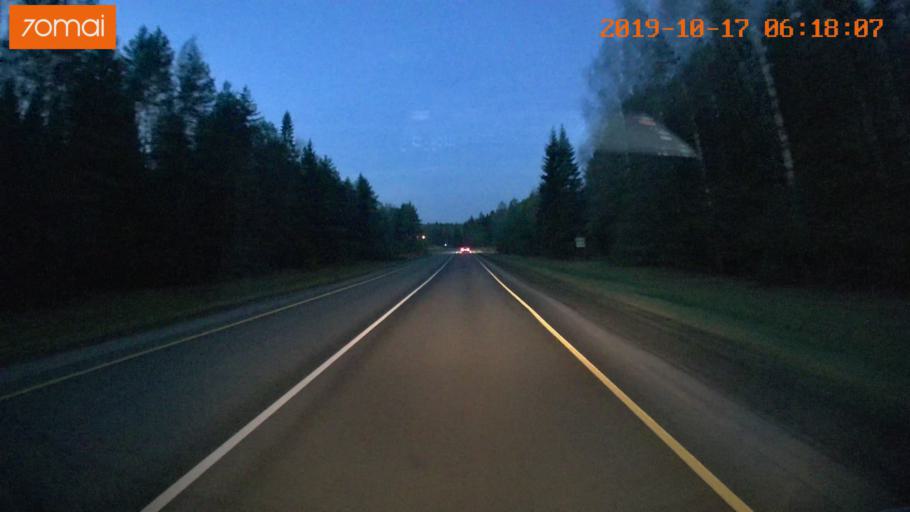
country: RU
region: Ivanovo
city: Lezhnevo
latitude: 56.8450
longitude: 40.9170
